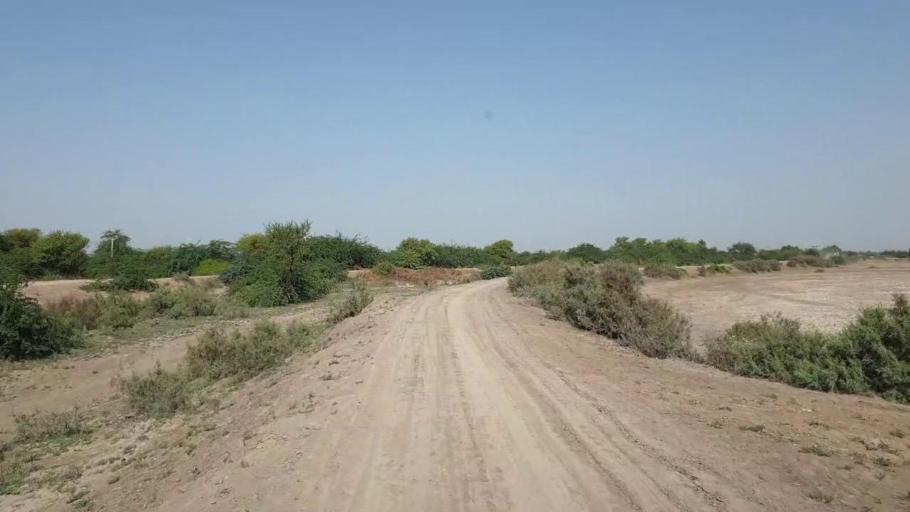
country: PK
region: Sindh
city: Tando Bago
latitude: 24.6636
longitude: 69.0673
